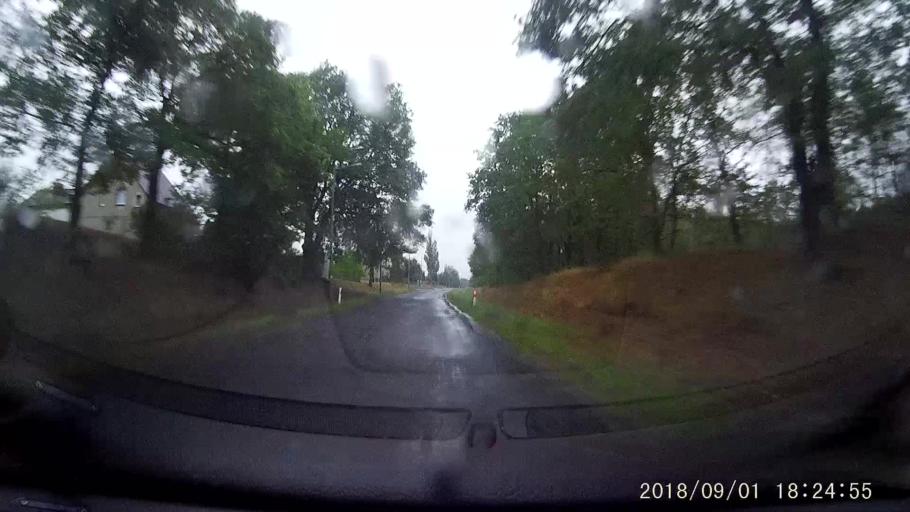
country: PL
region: Lower Silesian Voivodeship
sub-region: Powiat zgorzelecki
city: Piensk
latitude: 51.2332
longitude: 15.0337
